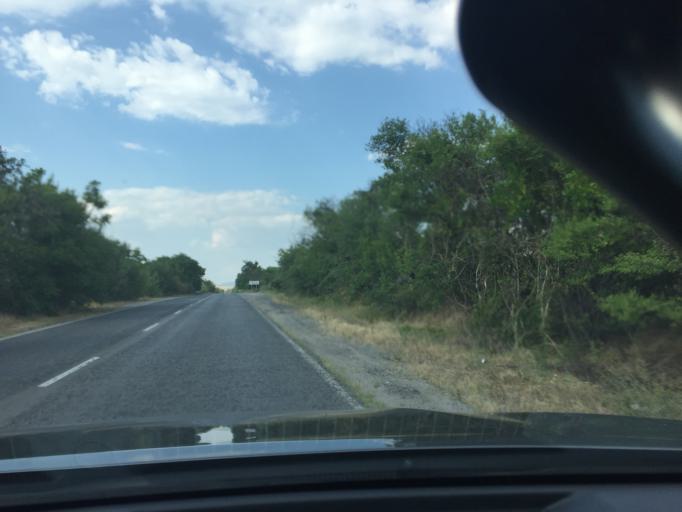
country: BG
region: Kyustendil
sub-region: Obshtina Boboshevo
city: Boboshevo
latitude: 42.1432
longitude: 23.0398
